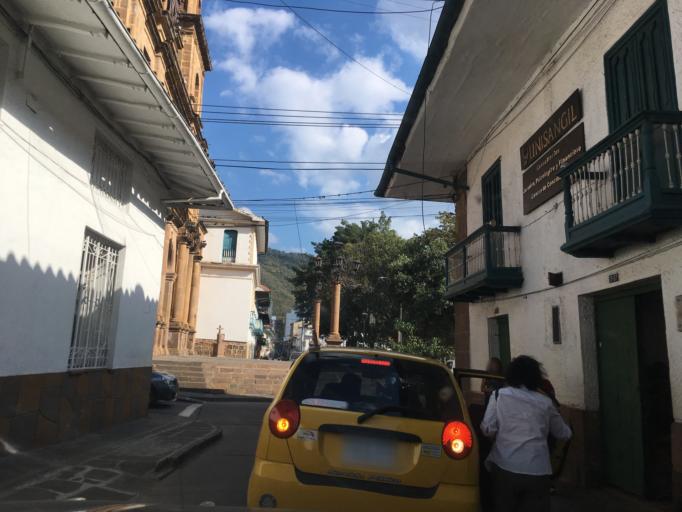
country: CO
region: Santander
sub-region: San Gil
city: San Gil
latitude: 6.5555
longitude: -73.1339
